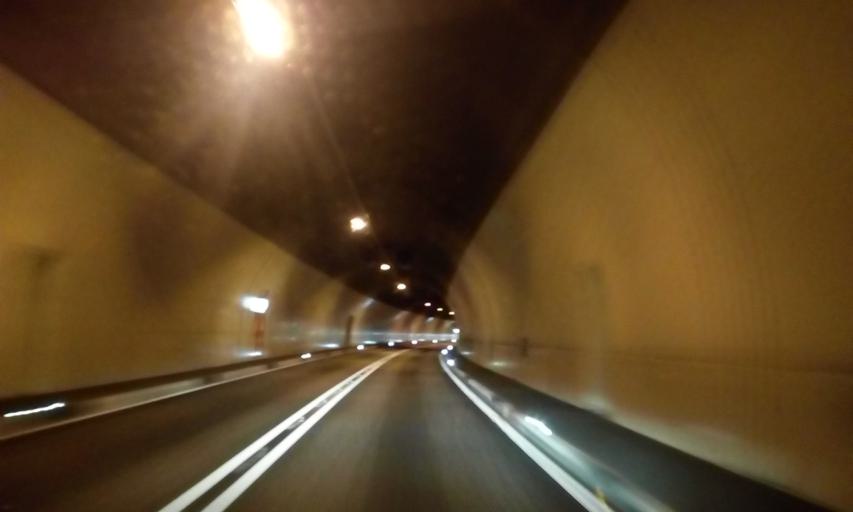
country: CH
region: Grisons
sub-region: Hinterrhein District
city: Thusis
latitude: 46.6986
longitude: 9.4581
